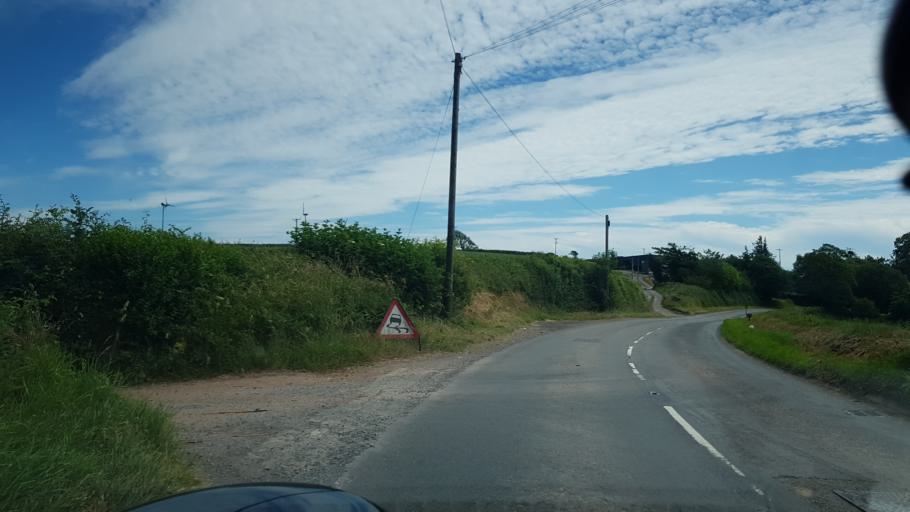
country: GB
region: Wales
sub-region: Carmarthenshire
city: Saint Clears
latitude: 51.7832
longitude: -4.4726
